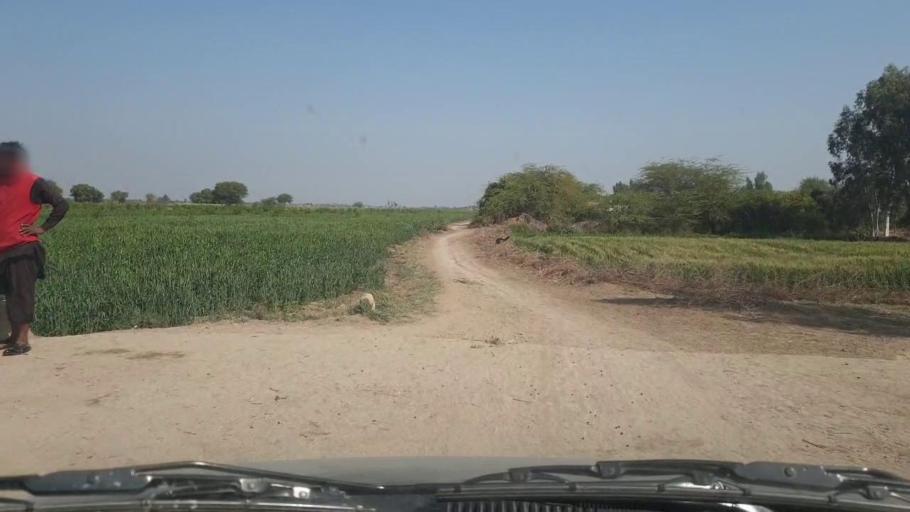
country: PK
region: Sindh
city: Samaro
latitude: 25.2812
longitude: 69.3147
